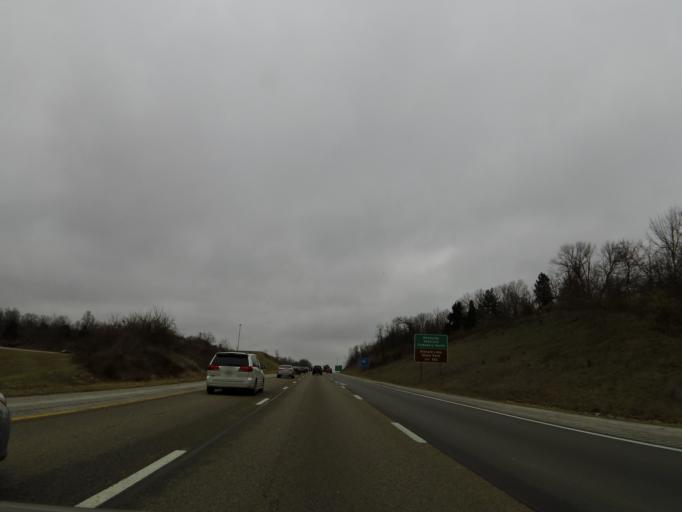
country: US
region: Kentucky
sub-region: Grant County
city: Williamstown
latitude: 38.6335
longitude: -84.5800
